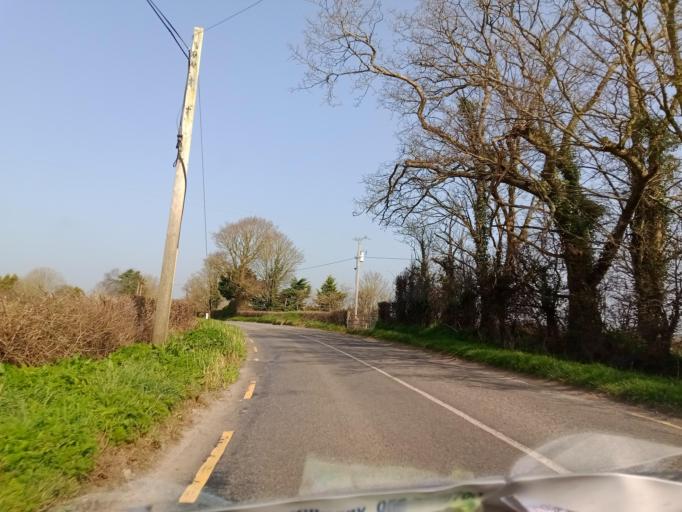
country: IE
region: Leinster
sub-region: Kilkenny
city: Callan
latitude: 52.5111
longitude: -7.3845
